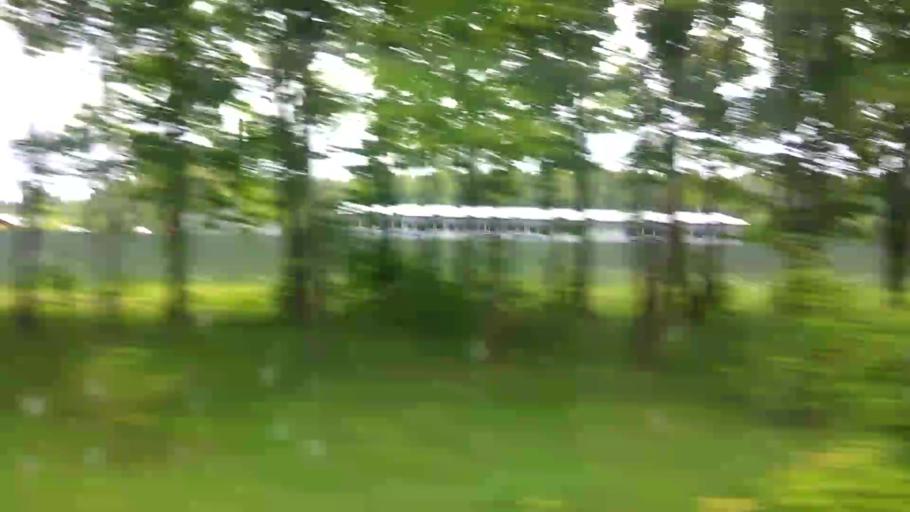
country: RU
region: Moskovskaya
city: Ozherel'ye
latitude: 54.8389
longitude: 38.2737
